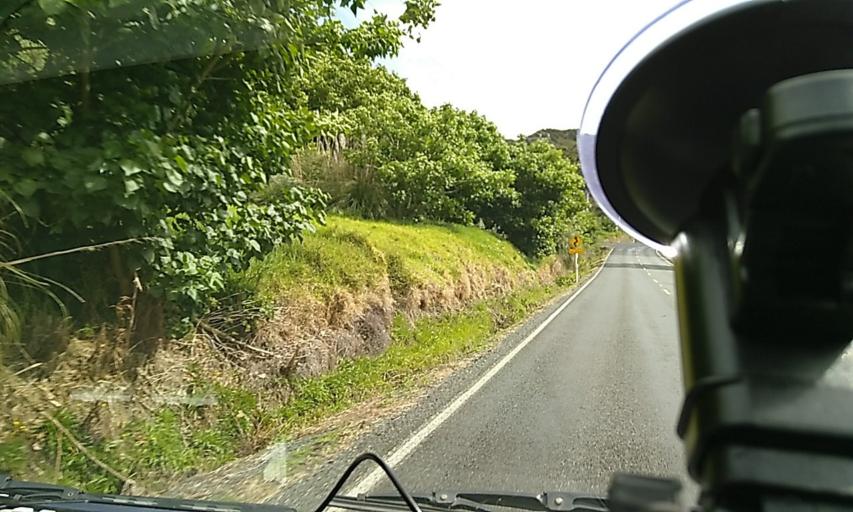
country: NZ
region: Northland
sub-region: Far North District
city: Ahipara
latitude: -35.5358
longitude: 173.3871
